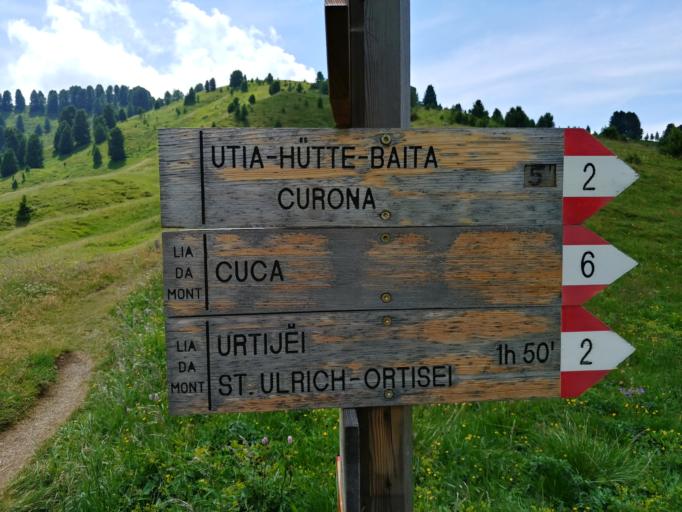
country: IT
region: Trentino-Alto Adige
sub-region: Bolzano
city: Santa Cristina Valgardena
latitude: 46.5874
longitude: 11.7240
